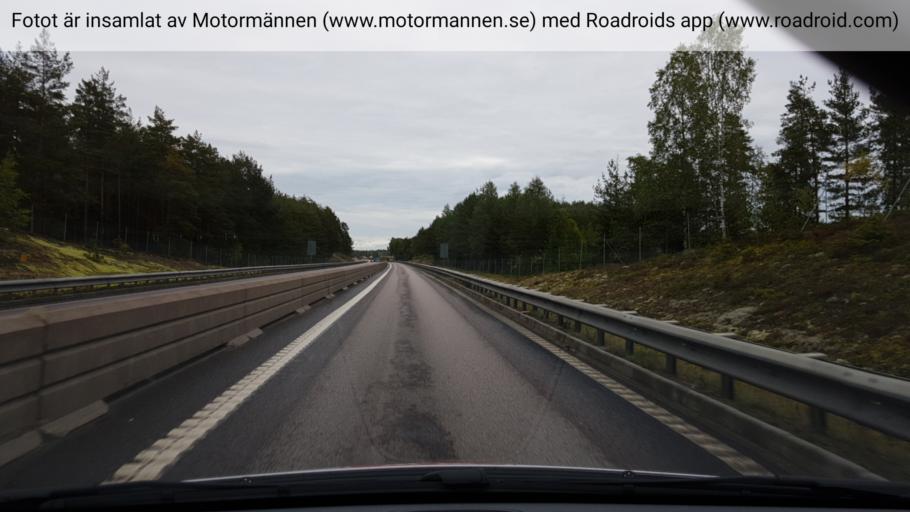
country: SE
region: Vaermland
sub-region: Karlstads Kommun
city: Edsvalla
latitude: 59.3875
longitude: 13.2428
